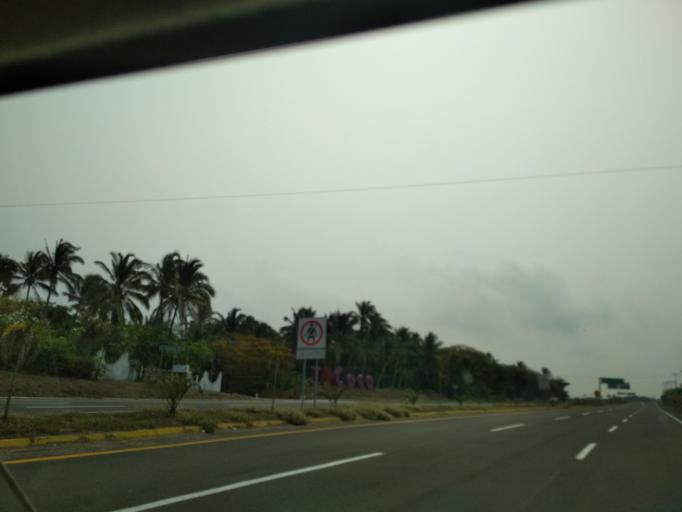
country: MX
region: Veracruz
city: Anton Lizardo
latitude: 19.0513
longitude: -96.0130
